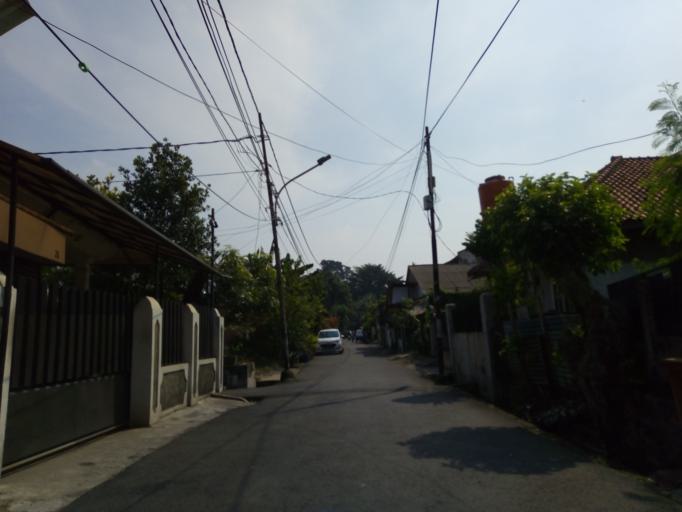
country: ID
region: Jakarta Raya
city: Jakarta
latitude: -6.2069
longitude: 106.8323
